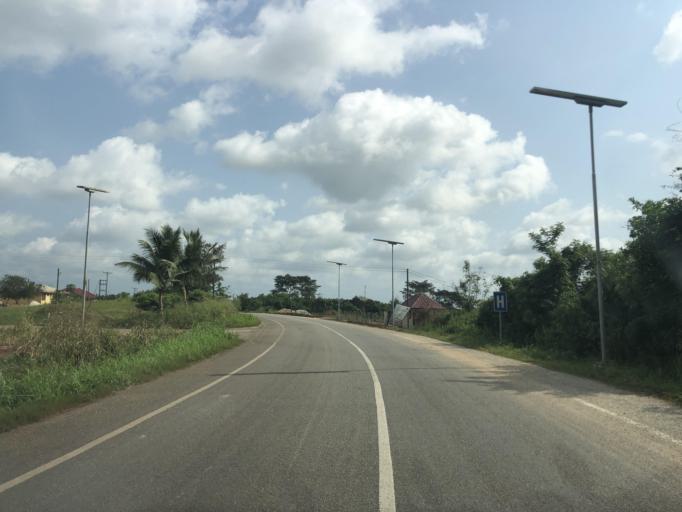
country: GH
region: Central
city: Elmina
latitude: 5.2114
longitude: -1.3233
